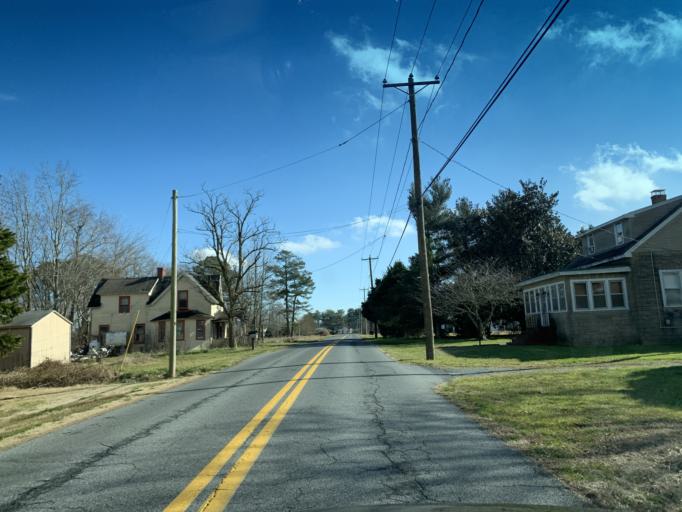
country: US
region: Delaware
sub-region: Sussex County
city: Selbyville
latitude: 38.4542
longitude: -75.2005
